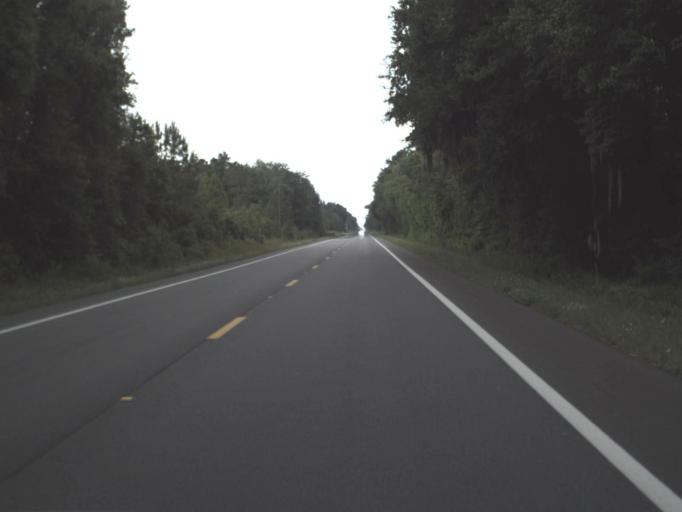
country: US
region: Florida
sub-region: Columbia County
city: Five Points
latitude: 30.4520
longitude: -82.6492
